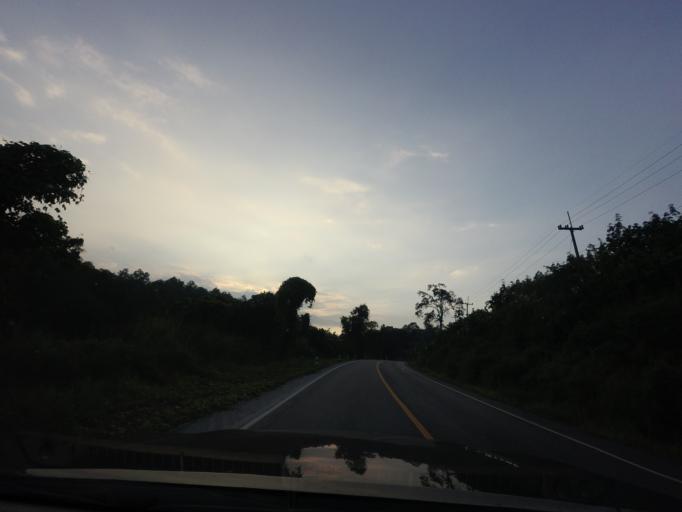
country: TH
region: Loei
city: Na Haeo
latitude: 17.4991
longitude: 101.0528
